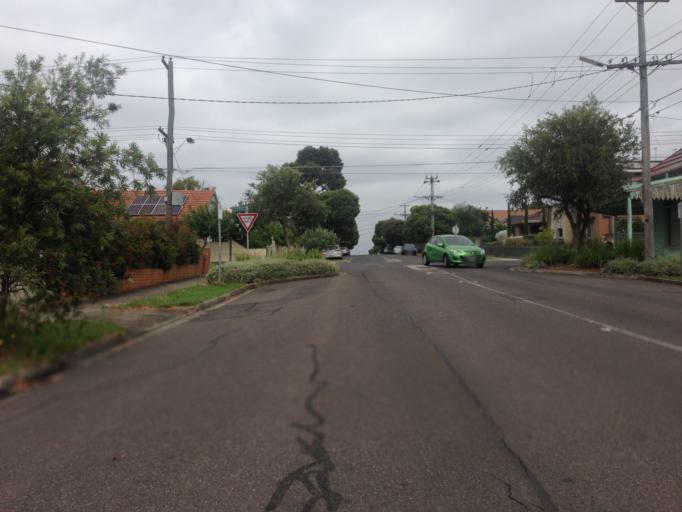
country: AU
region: Victoria
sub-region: Darebin
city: Thornbury
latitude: -37.7584
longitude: 145.0049
